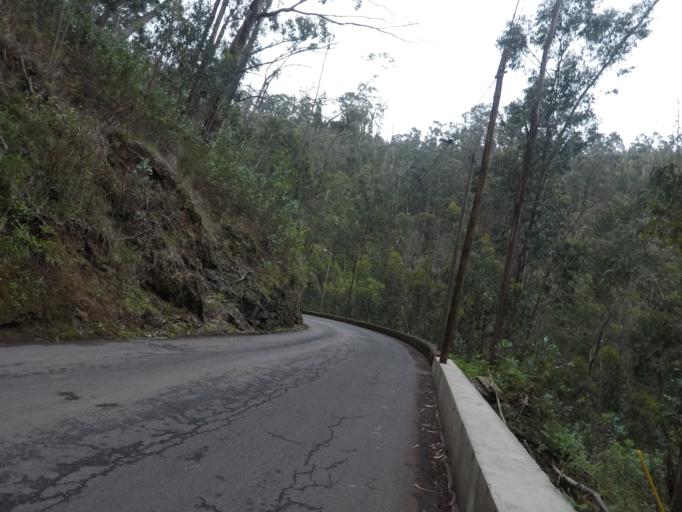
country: PT
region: Madeira
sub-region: Calheta
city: Estreito da Calheta
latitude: 32.7541
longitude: -17.1947
